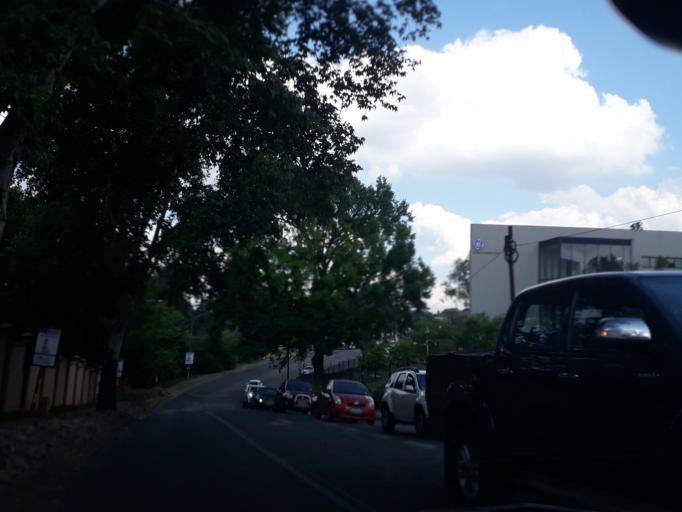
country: ZA
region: Gauteng
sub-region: City of Johannesburg Metropolitan Municipality
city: Johannesburg
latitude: -26.1466
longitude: 28.0557
